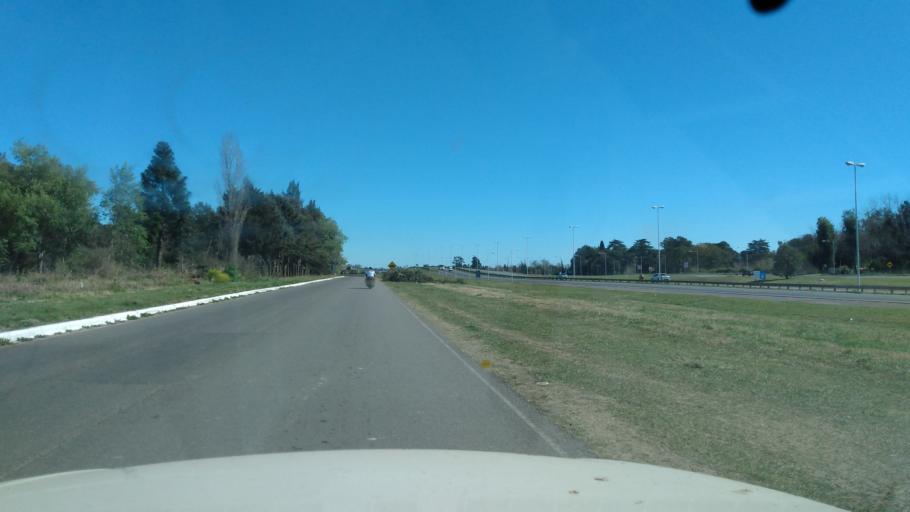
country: AR
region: Buenos Aires
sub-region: Partido de Lujan
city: Lujan
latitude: -34.5588
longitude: -59.0955
